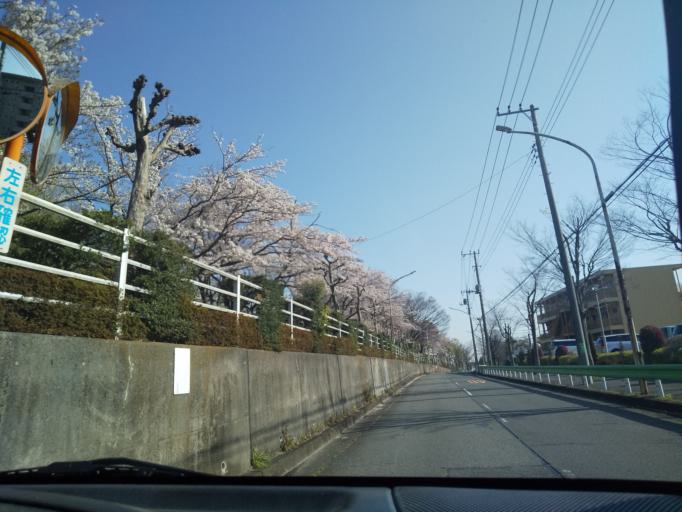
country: JP
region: Tokyo
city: Hino
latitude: 35.6526
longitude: 139.4222
